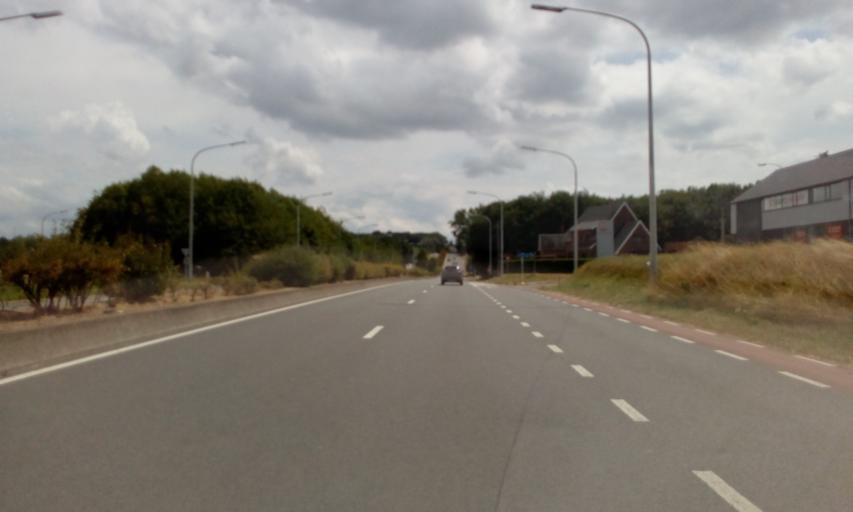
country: BE
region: Wallonia
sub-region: Province de Namur
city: Assesse
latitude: 50.4102
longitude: 4.9545
